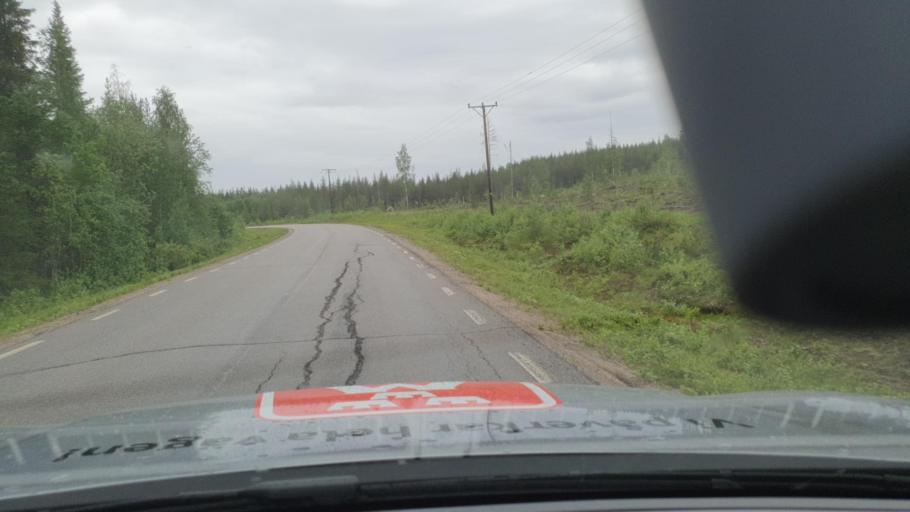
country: SE
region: Norrbotten
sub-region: Pajala Kommun
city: Pajala
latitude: 66.7717
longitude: 23.1456
